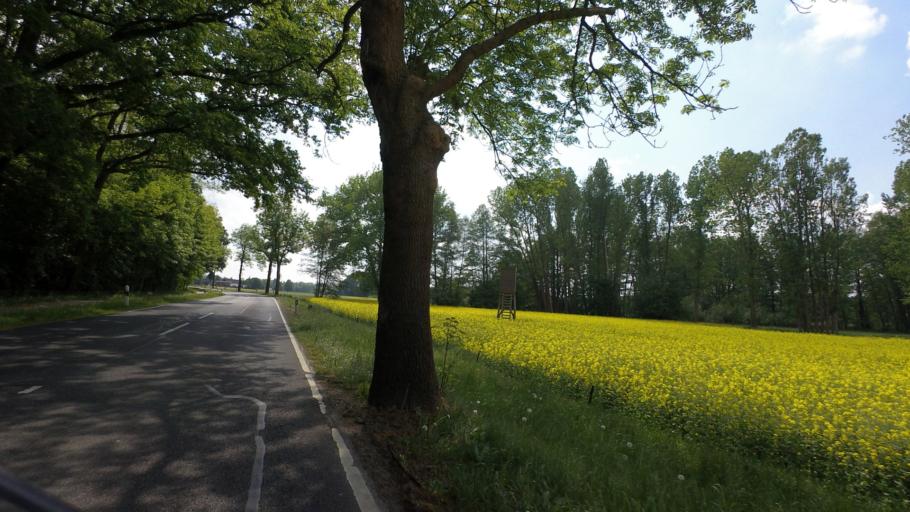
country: DE
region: Saxony
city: Rietschen
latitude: 51.4080
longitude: 14.7871
